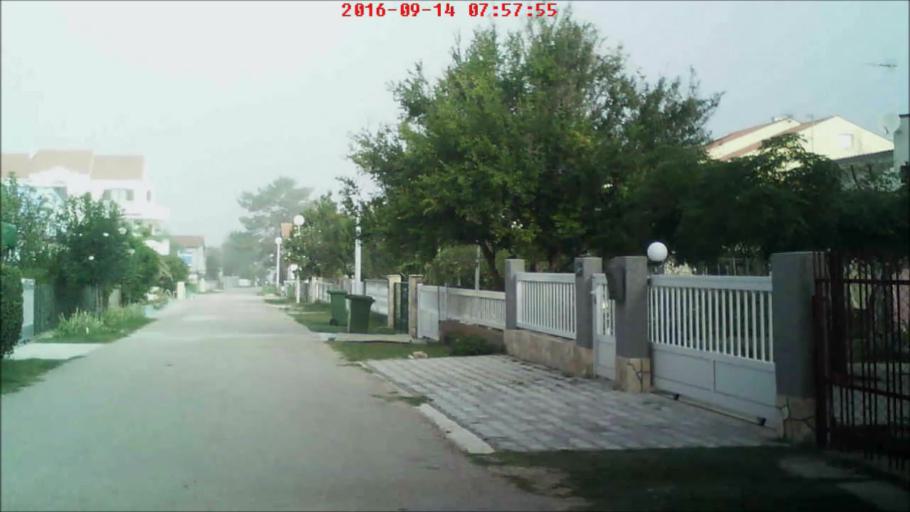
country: HR
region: Zadarska
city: Nin
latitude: 44.2589
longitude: 15.1632
